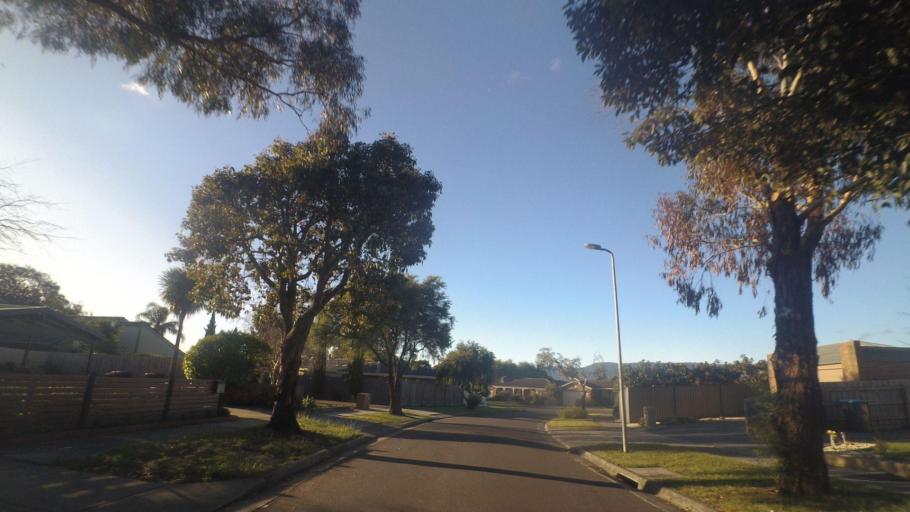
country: AU
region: Victoria
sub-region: Knox
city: Rowville
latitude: -37.9203
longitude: 145.2601
